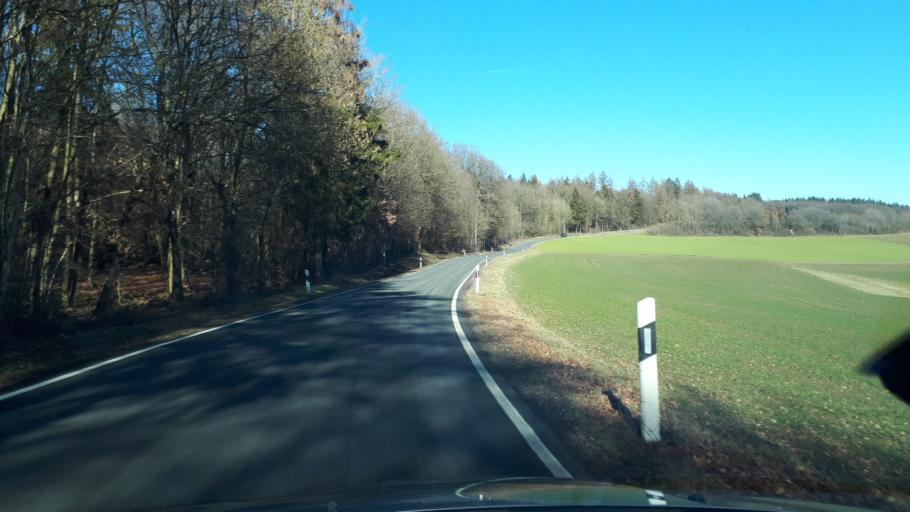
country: DE
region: Rheinland-Pfalz
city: Ellscheid
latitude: 50.1642
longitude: 6.9136
